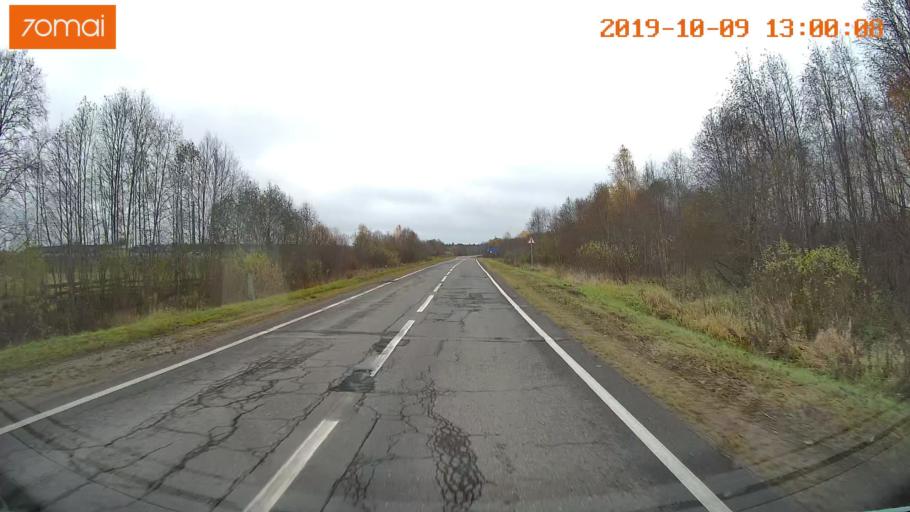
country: RU
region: Jaroslavl
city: Prechistoye
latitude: 58.3801
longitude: 40.4754
